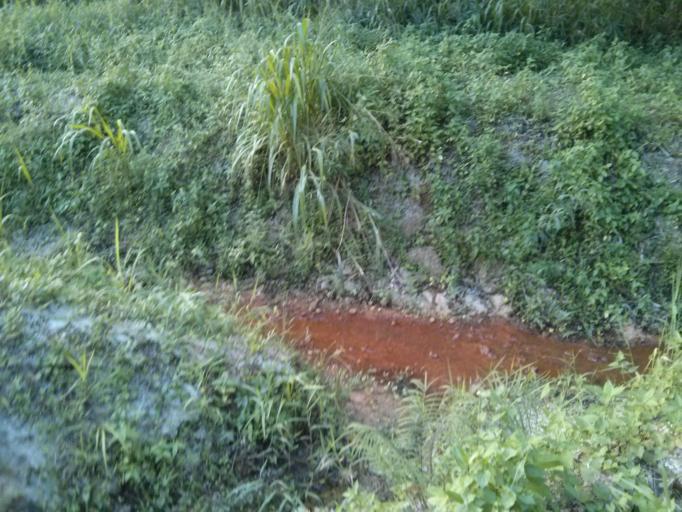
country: MY
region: Johor
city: Kampung Pasir Gudang Baru
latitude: 1.4327
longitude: 103.8598
